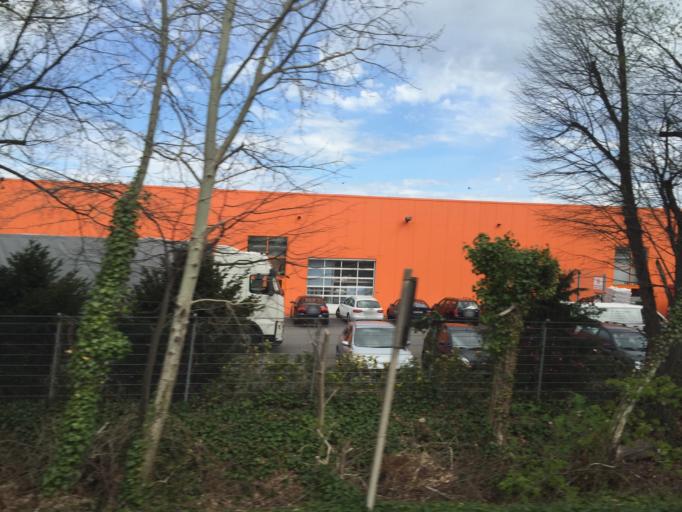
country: DE
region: Saxony
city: Bautzen
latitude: 51.1779
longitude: 14.3969
